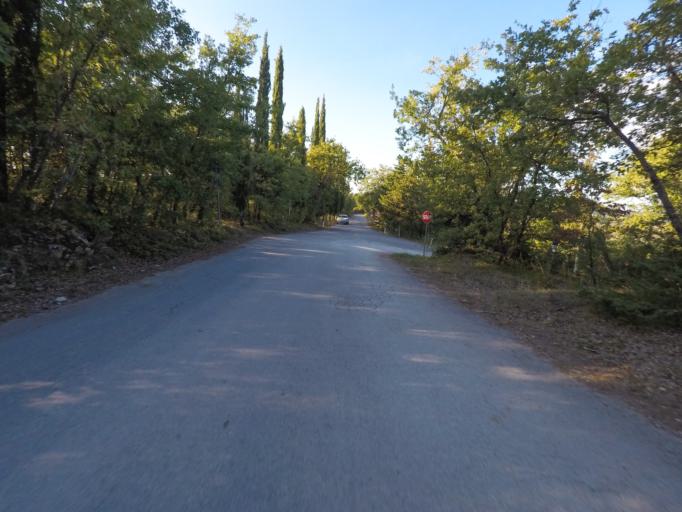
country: IT
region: Tuscany
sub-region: Provincia di Siena
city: Gaiole in Chianti
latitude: 43.4419
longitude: 11.3949
